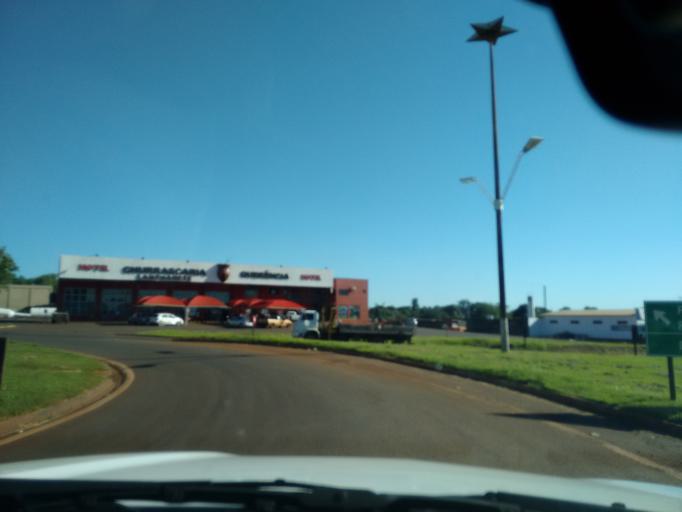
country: BR
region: Mato Grosso do Sul
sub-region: Dourados
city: Dourados
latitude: -22.2591
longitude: -54.8036
